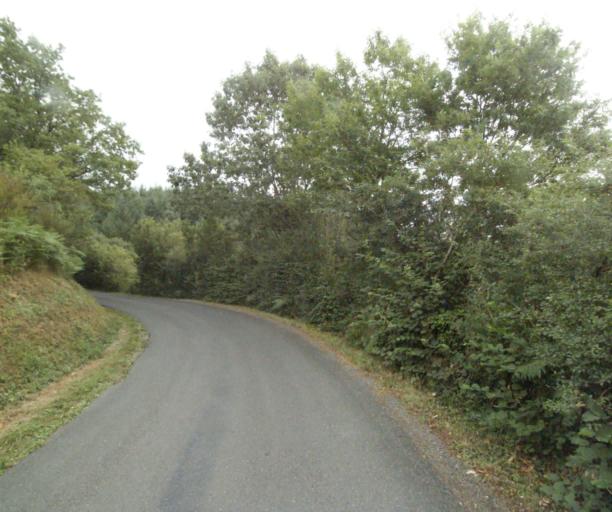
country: FR
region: Midi-Pyrenees
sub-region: Departement du Tarn
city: Soreze
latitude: 43.4127
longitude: 2.0588
